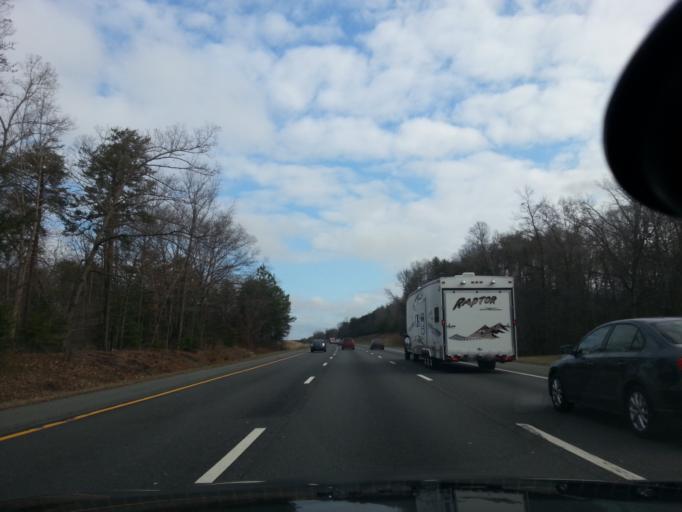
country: US
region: Virginia
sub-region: Spotsylvania County
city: Spotsylvania Courthouse
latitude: 38.1729
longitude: -77.5029
